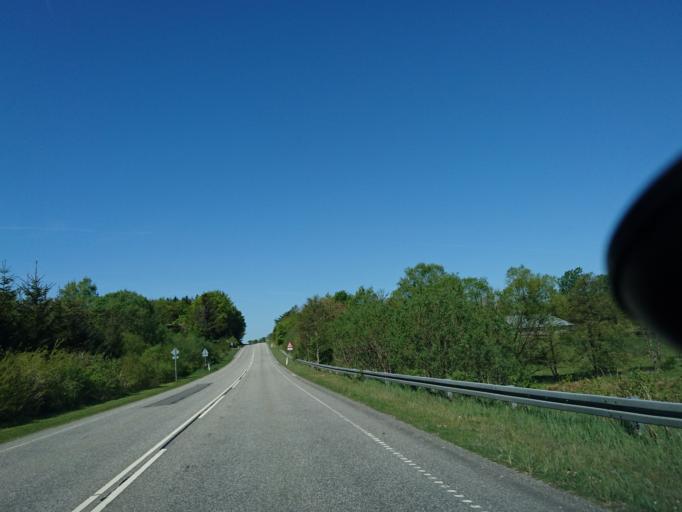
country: DK
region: North Denmark
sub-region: Hjorring Kommune
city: Sindal
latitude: 57.4643
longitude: 10.2804
